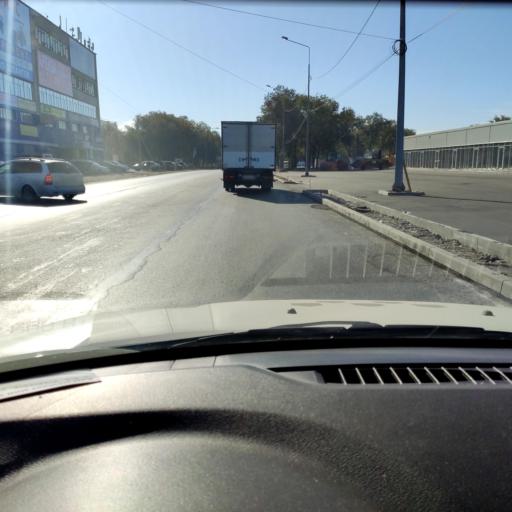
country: RU
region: Samara
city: Tol'yatti
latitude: 53.5698
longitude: 49.4589
